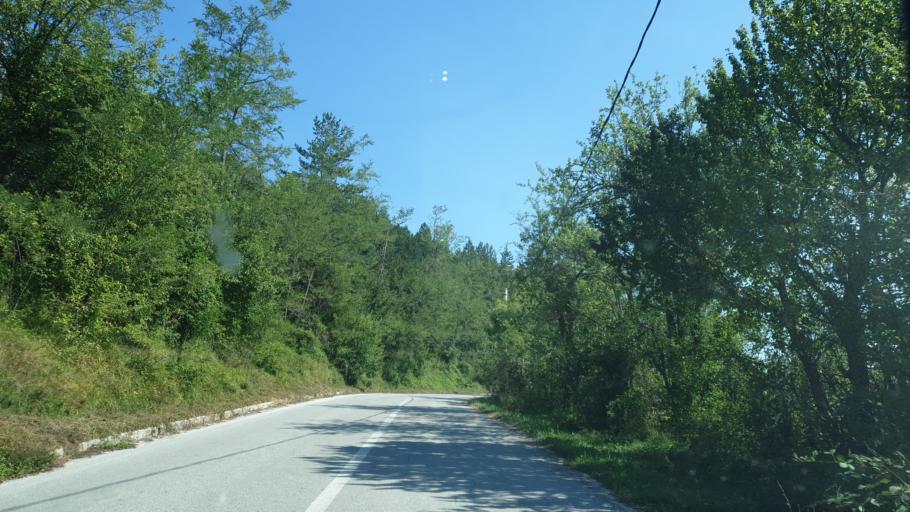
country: RS
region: Central Serbia
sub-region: Zlatiborski Okrug
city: Cajetina
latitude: 43.6767
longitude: 19.8306
